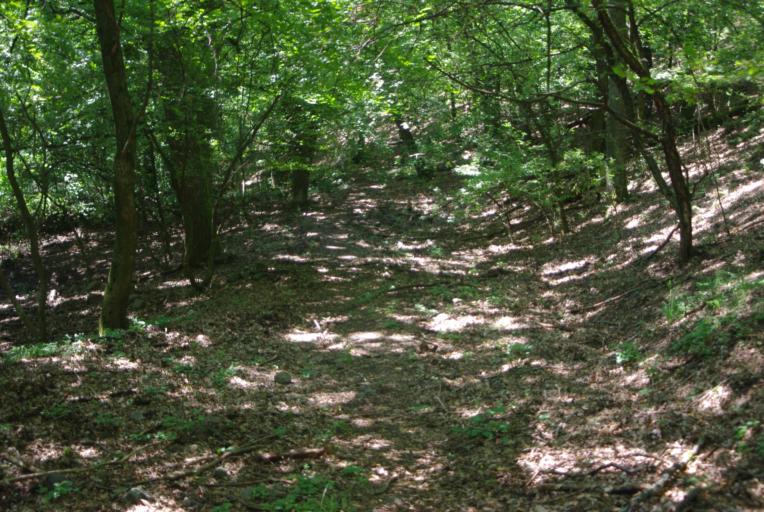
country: HU
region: Borsod-Abauj-Zemplen
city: Gonc
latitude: 48.4052
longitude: 21.3023
